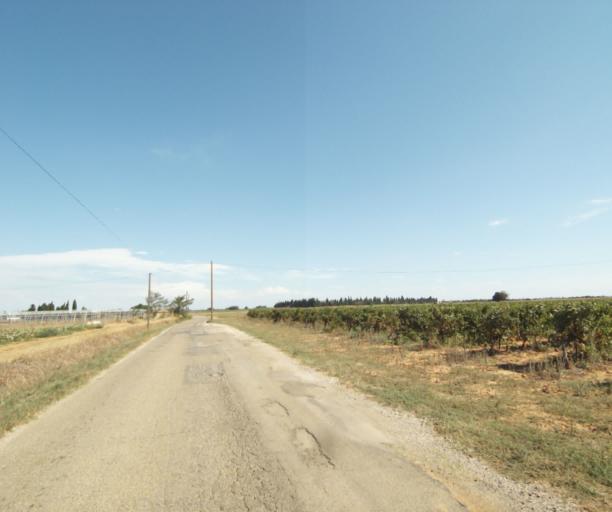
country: FR
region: Languedoc-Roussillon
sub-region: Departement du Gard
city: Manduel
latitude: 43.7996
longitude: 4.4555
